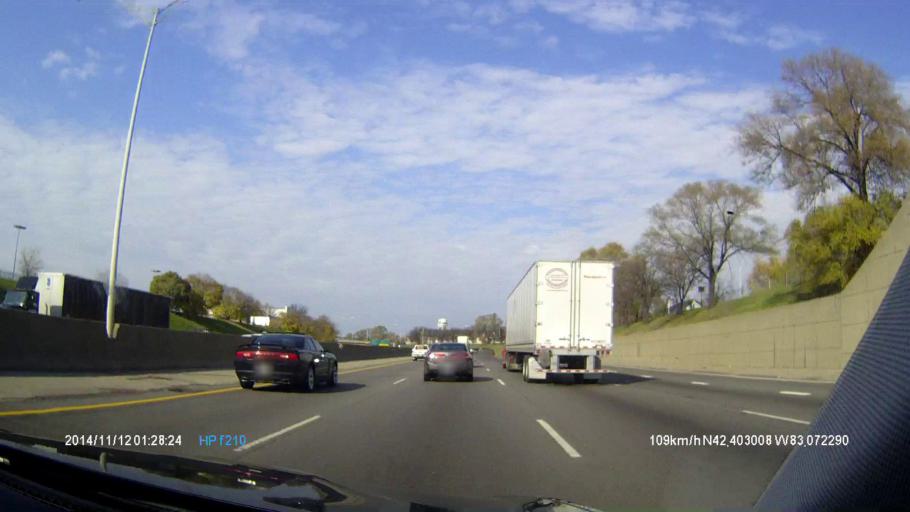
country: US
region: Michigan
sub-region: Wayne County
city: Highland Park
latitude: 42.4034
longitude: -83.0726
